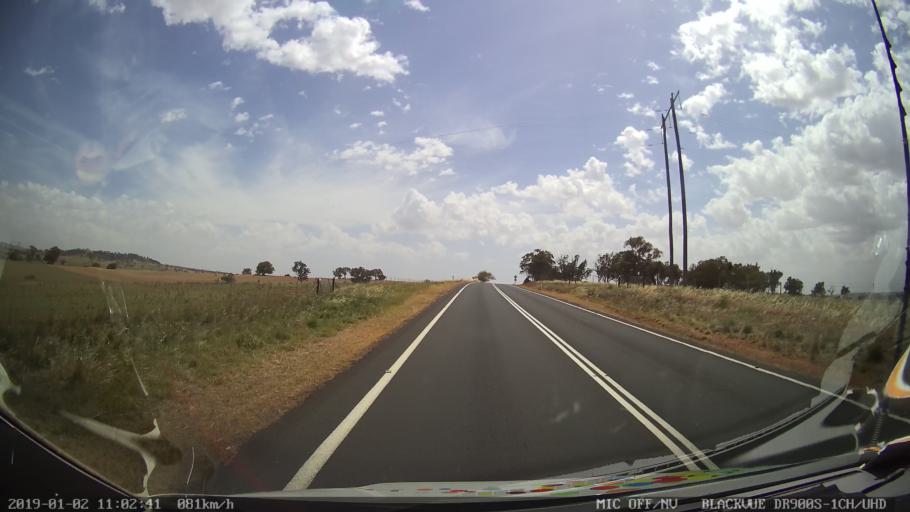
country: AU
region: New South Wales
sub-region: Young
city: Young
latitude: -34.5834
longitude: 148.3290
